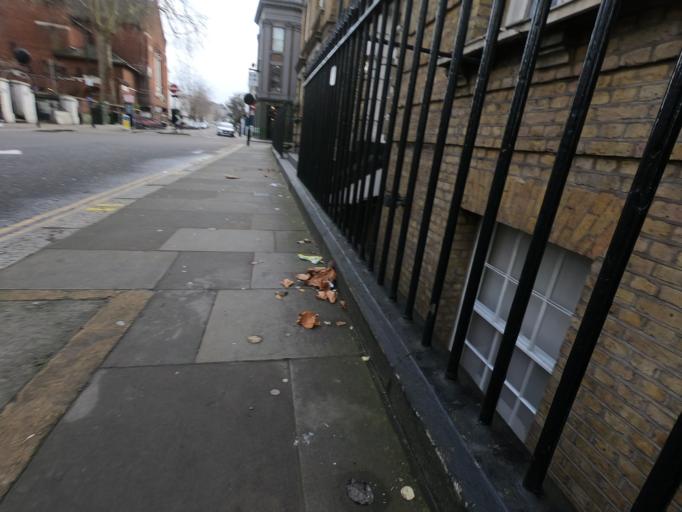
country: GB
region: England
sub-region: Greater London
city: Kensington
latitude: 51.5088
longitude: -0.1938
